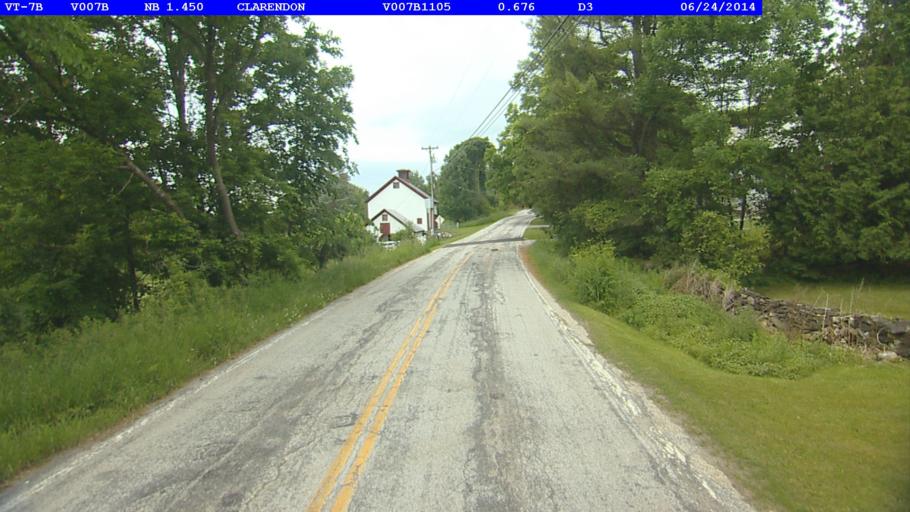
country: US
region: Vermont
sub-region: Rutland County
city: Rutland
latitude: 43.5049
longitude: -72.9703
